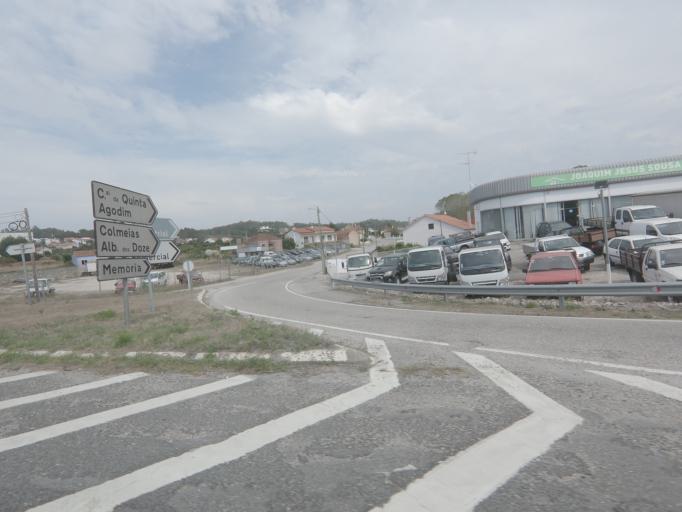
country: PT
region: Leiria
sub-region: Leiria
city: Caranguejeira
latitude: 39.8072
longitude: -8.7420
